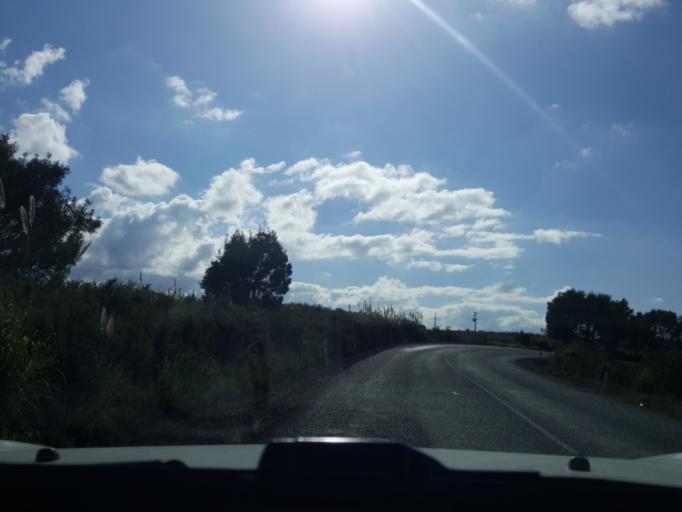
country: NZ
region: Waikato
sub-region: Waikato District
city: Ngaruawahia
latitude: -37.5386
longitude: 175.1753
